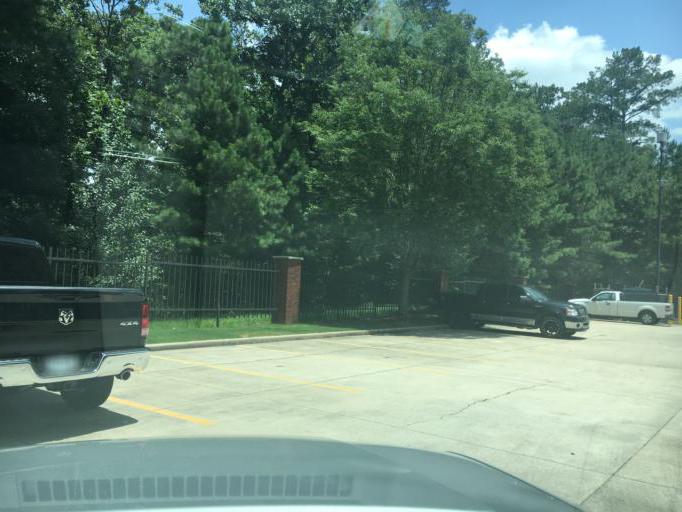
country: US
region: Alabama
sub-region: Jefferson County
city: Cahaba Heights
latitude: 33.4414
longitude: -86.7248
